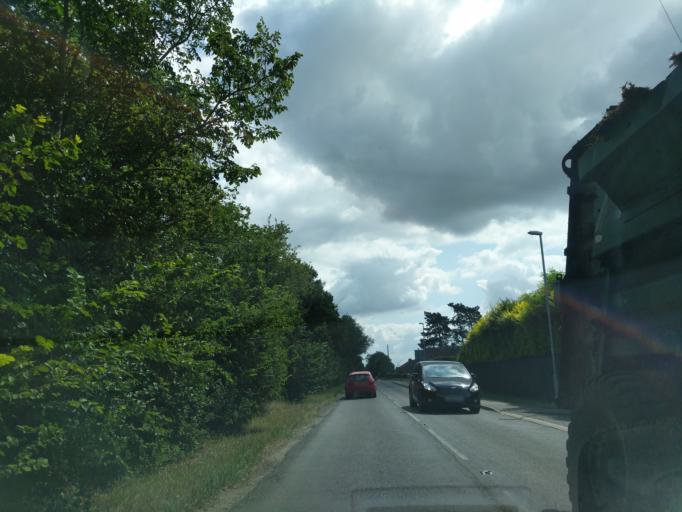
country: GB
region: England
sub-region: Cambridgeshire
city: Isleham
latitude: 52.3116
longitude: 0.4113
